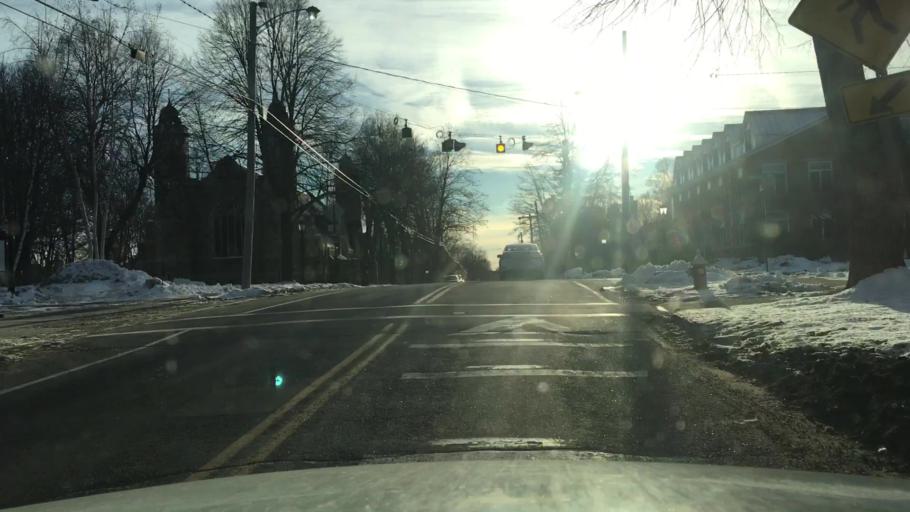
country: US
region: Maine
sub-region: Androscoggin County
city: Lewiston
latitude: 44.1073
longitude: -70.2054
